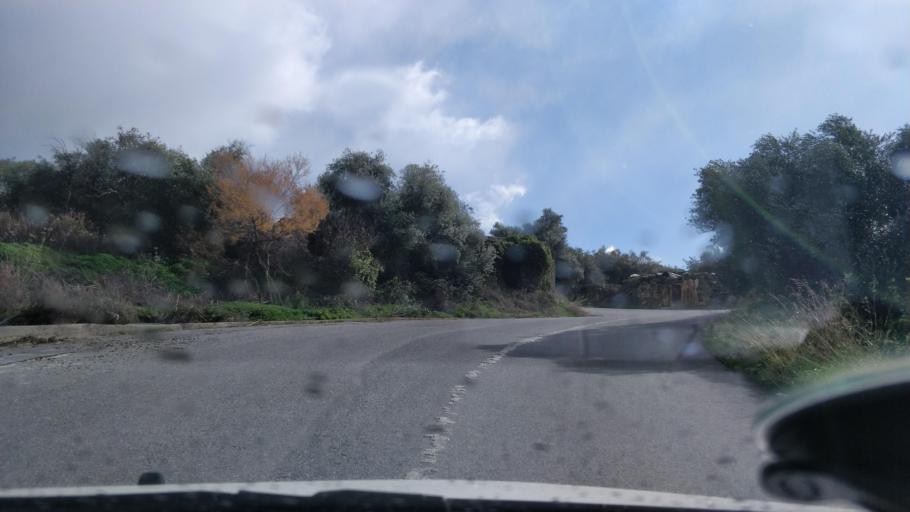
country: GR
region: Crete
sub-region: Nomos Lasithiou
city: Gra Liyia
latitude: 34.9957
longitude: 25.5083
